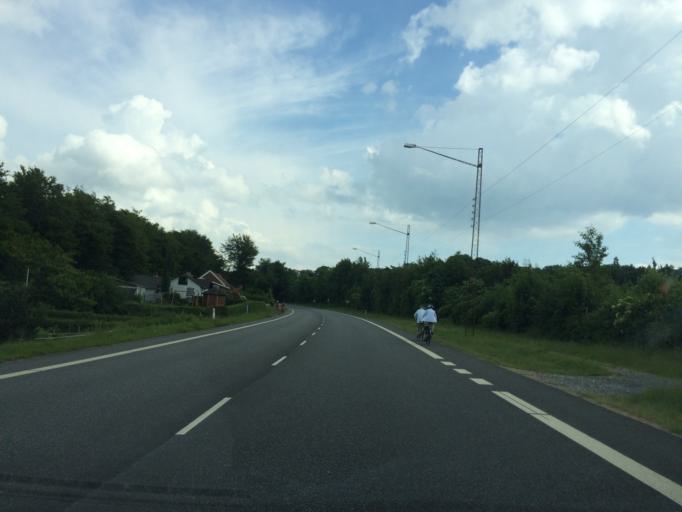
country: DK
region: South Denmark
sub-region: Fredericia Kommune
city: Snoghoj
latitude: 55.5049
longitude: 9.7044
